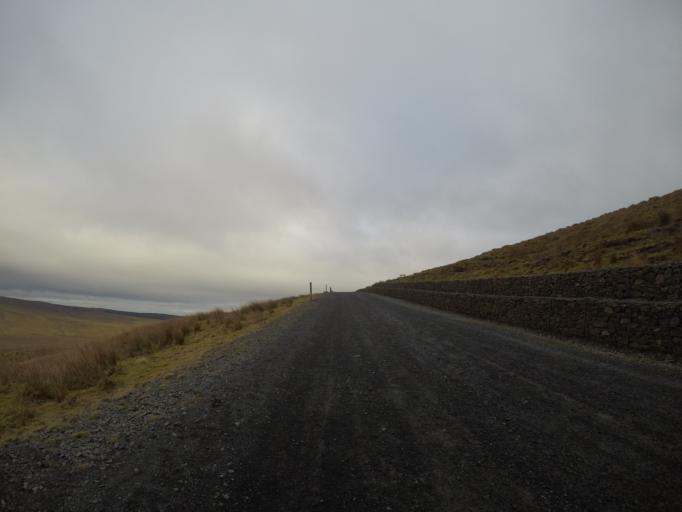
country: GB
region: Scotland
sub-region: North Ayrshire
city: Fairlie
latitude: 55.7635
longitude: -4.7948
